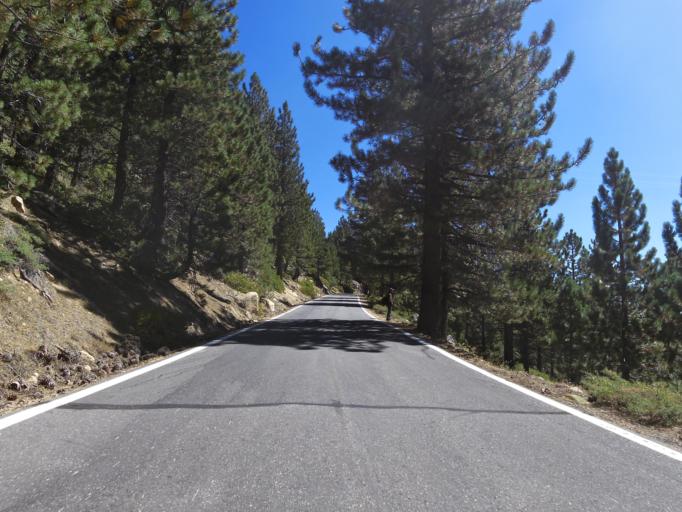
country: US
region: Nevada
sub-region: Douglas County
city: Gardnerville Ranchos
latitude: 38.5492
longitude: -119.8459
